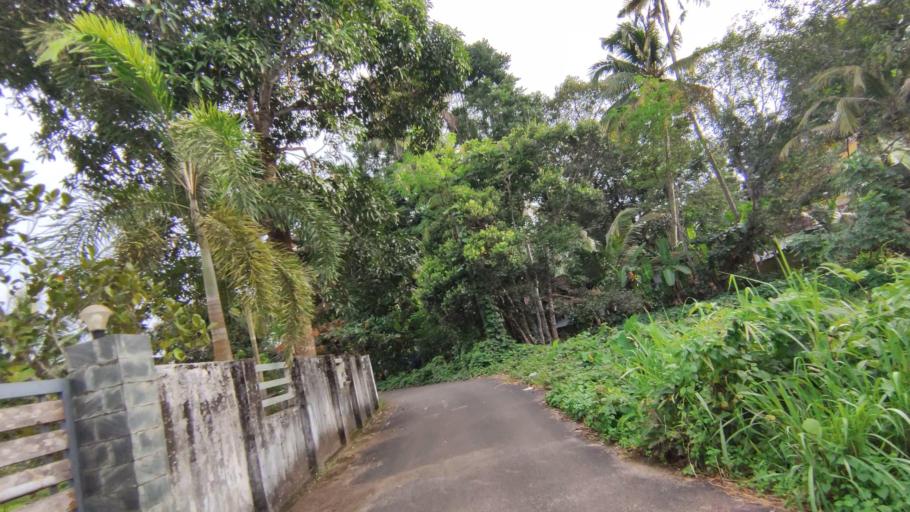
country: IN
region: Kerala
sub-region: Alappuzha
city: Shertallai
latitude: 9.6205
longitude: 76.3362
